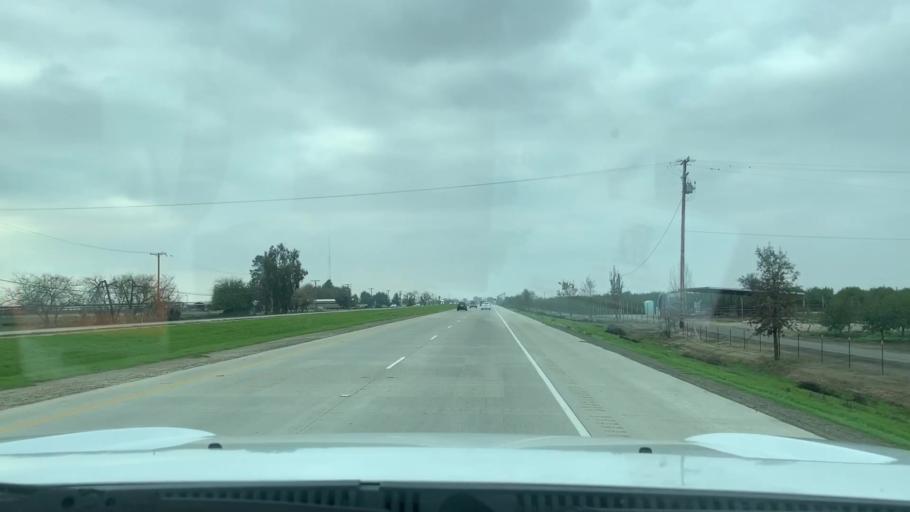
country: US
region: California
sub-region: Kings County
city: Home Garden
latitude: 36.3286
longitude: -119.5555
